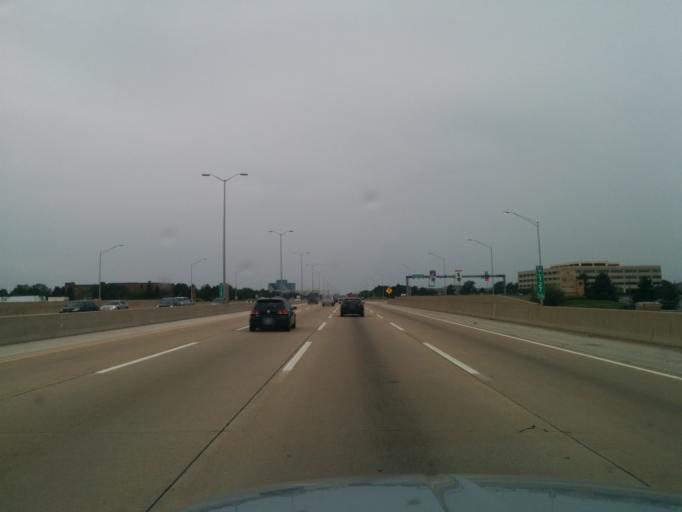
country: US
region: Illinois
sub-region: DuPage County
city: Naperville
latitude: 41.8063
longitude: -88.1270
